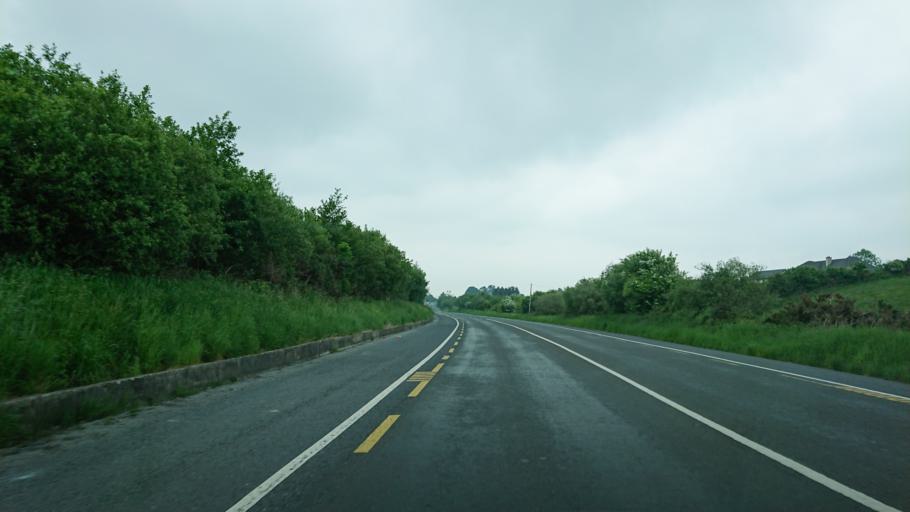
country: IE
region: Munster
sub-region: Waterford
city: Tra Mhor
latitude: 52.1863
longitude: -7.1292
